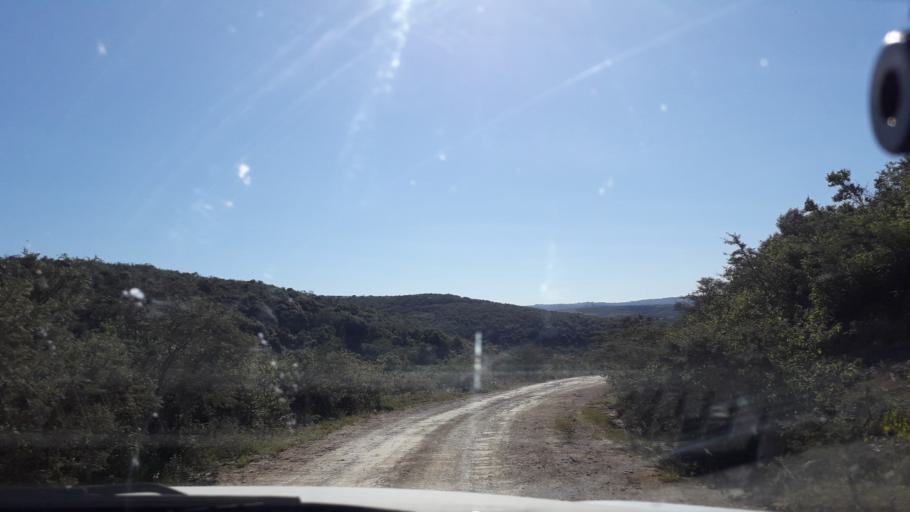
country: ZA
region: Eastern Cape
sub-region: Amathole District Municipality
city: Komga
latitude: -32.7757
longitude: 27.9594
